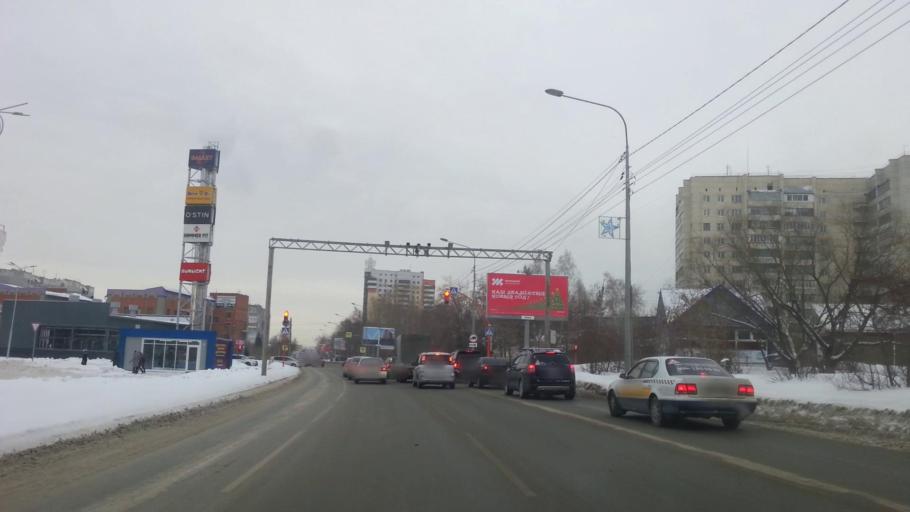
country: RU
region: Altai Krai
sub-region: Gorod Barnaulskiy
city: Barnaul
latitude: 53.3429
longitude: 83.7547
